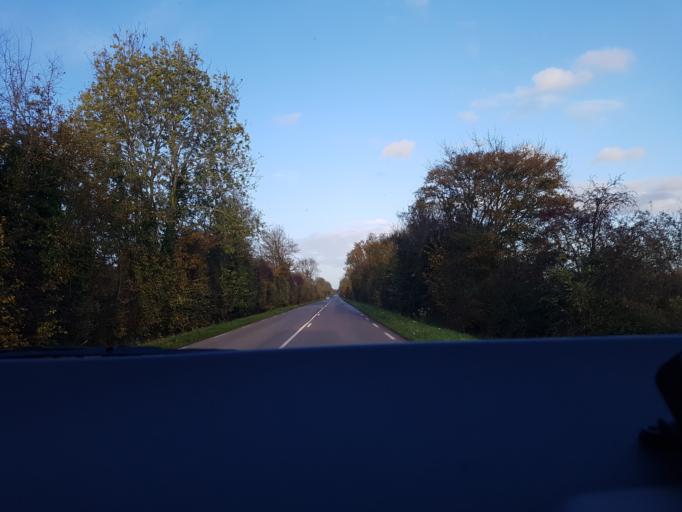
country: FR
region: Lower Normandy
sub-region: Departement du Calvados
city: Troarn
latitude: 49.1891
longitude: -0.1519
